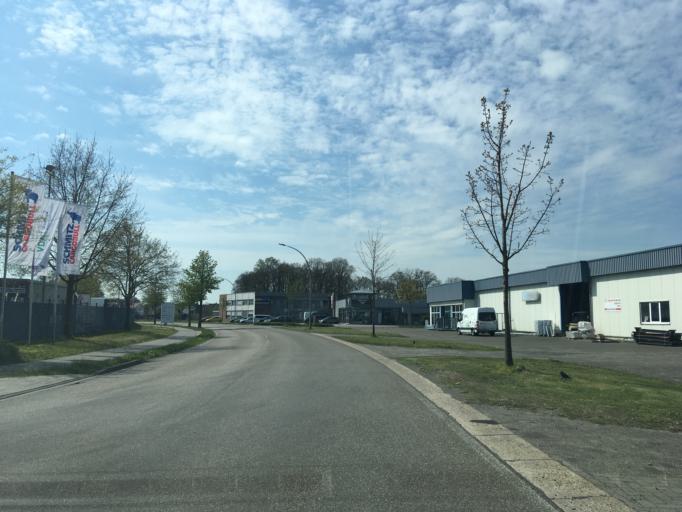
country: DE
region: North Rhine-Westphalia
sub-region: Regierungsbezirk Munster
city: Vreden
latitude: 52.0250
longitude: 6.8231
